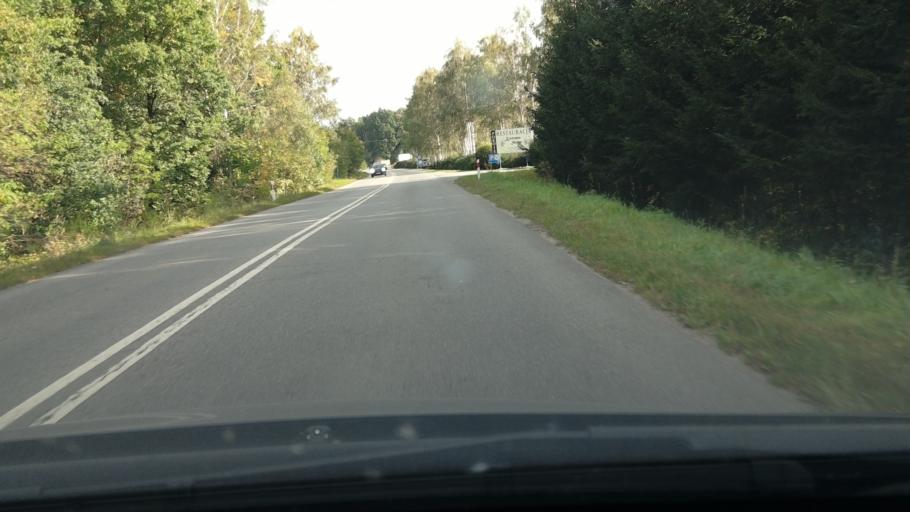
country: PL
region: Lower Silesian Voivodeship
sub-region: Powiat jeleniogorski
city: Myslakowice
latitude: 50.8106
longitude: 15.7680
